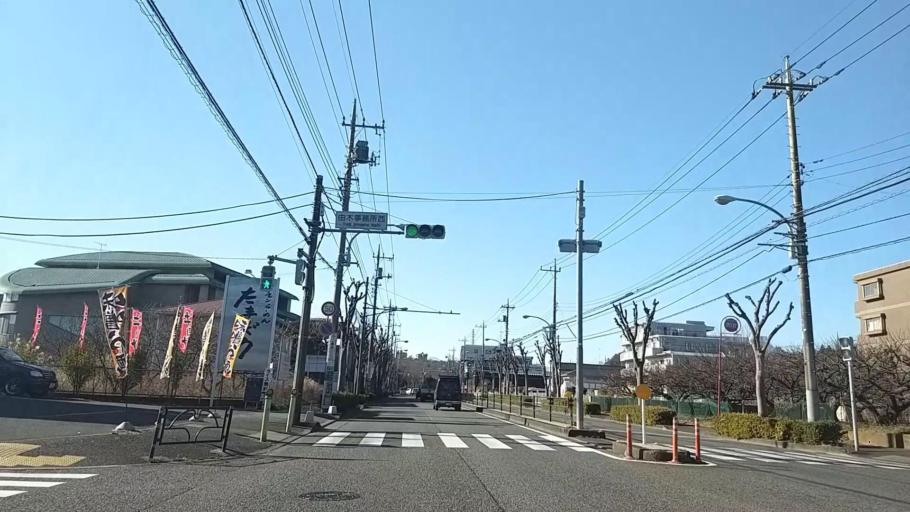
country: JP
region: Tokyo
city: Hino
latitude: 35.6258
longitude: 139.3795
